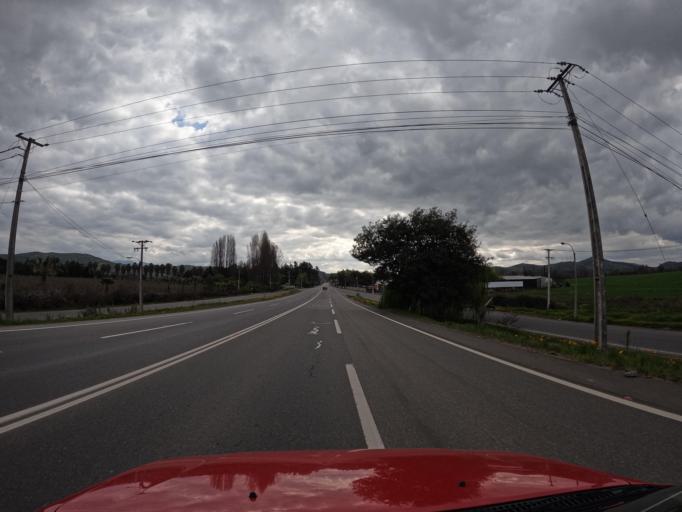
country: CL
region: Maule
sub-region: Provincia de Linares
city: San Javier
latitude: -35.6249
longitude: -71.7506
